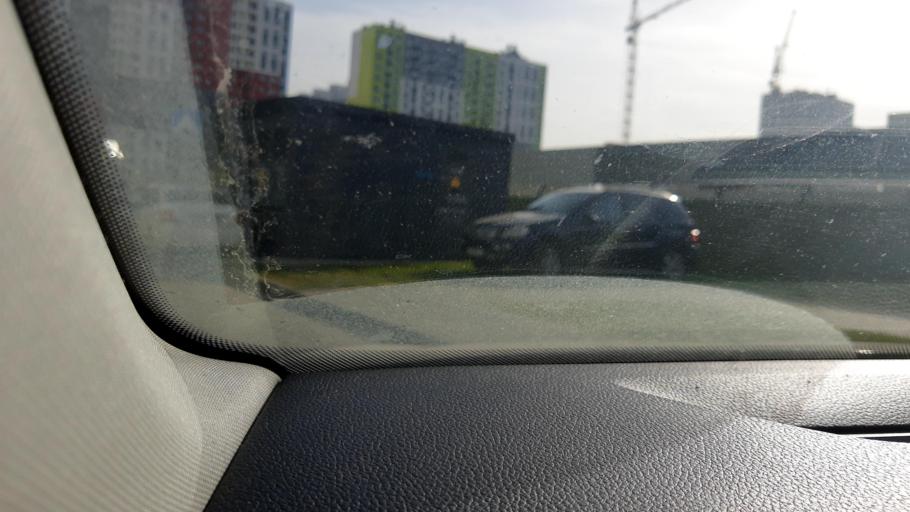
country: RU
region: Moskovskaya
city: Shcherbinka
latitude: 55.5263
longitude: 37.5843
